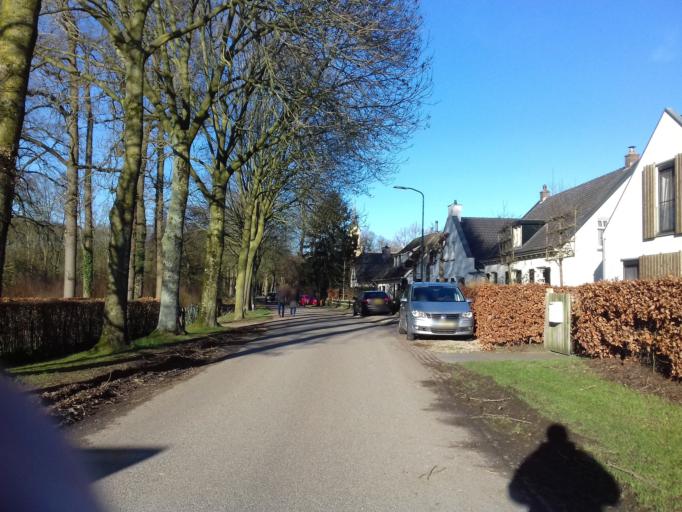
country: NL
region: Gelderland
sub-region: Gemeente Neerijnen
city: Neerijnen
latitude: 51.8300
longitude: 5.2794
